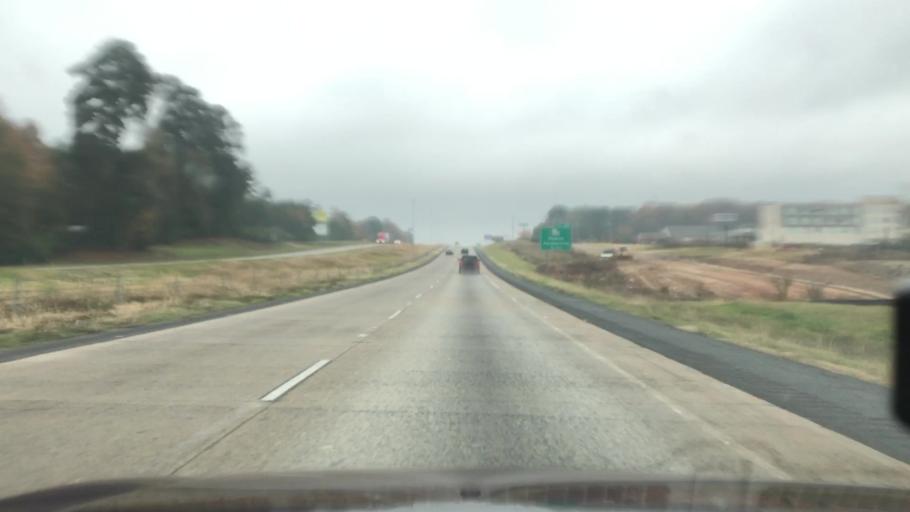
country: US
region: Louisiana
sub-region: Lincoln Parish
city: Ruston
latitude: 32.5405
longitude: -92.6039
